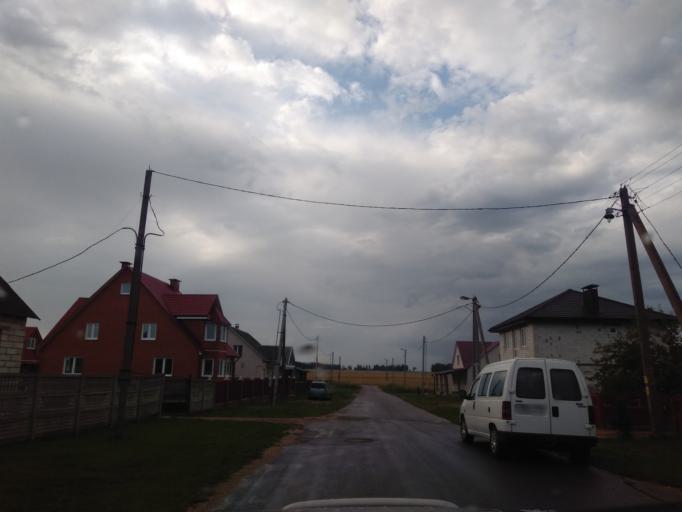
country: BY
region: Minsk
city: Kapyl'
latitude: 53.1662
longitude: 27.0801
